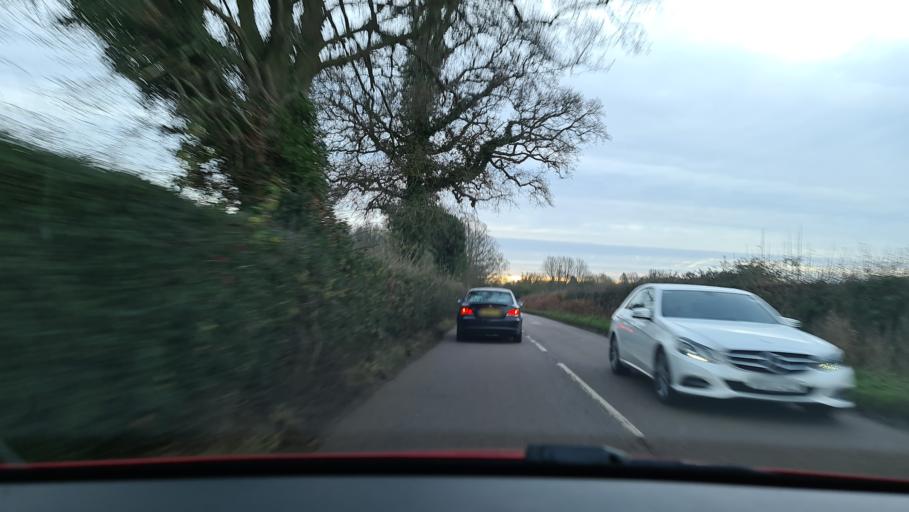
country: GB
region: England
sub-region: Buckinghamshire
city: Great Missenden
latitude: 51.6971
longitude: -0.6619
